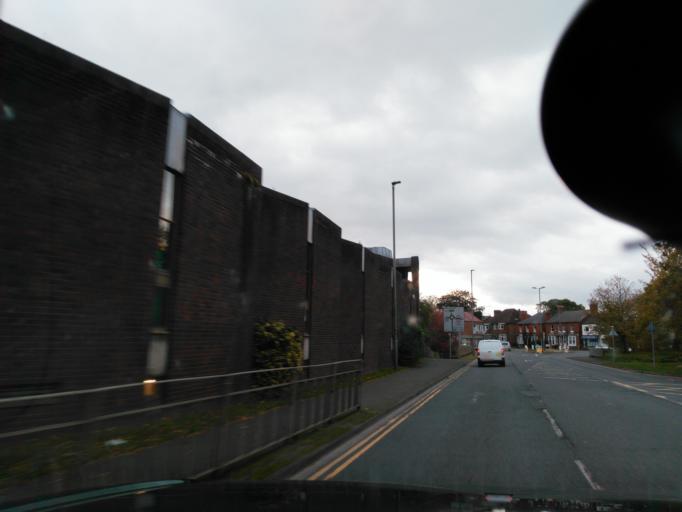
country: GB
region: England
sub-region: North Yorkshire
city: Northallerton
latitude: 54.3367
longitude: -1.4323
